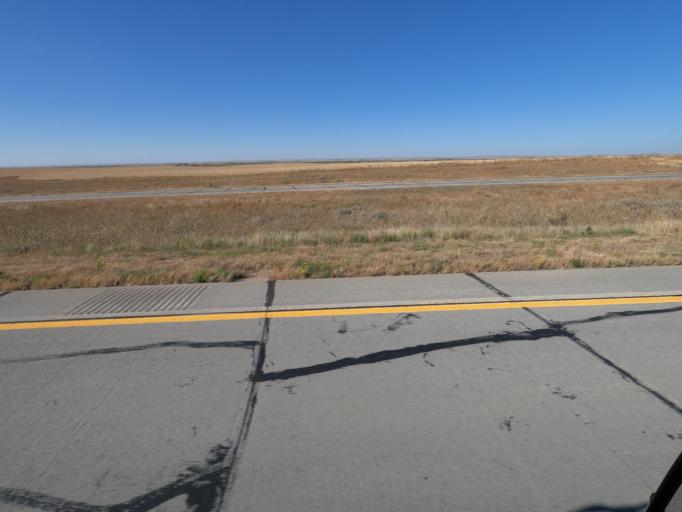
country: US
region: Colorado
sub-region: Logan County
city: Sterling
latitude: 40.7835
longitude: -102.9076
